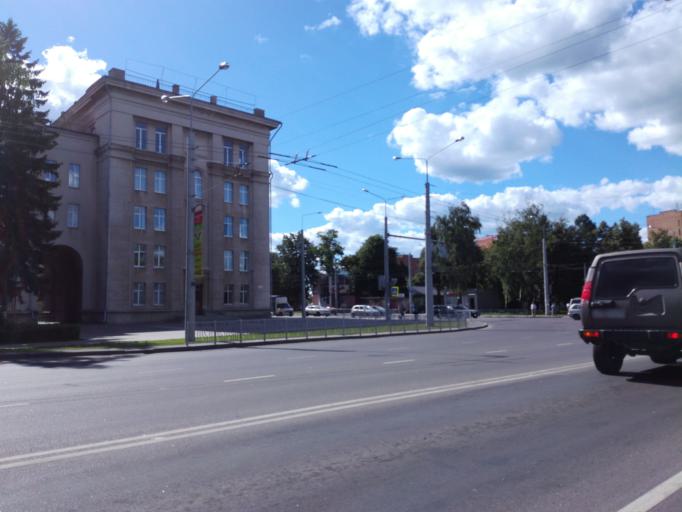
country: RU
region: Kursk
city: Kursk
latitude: 51.7654
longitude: 36.1836
